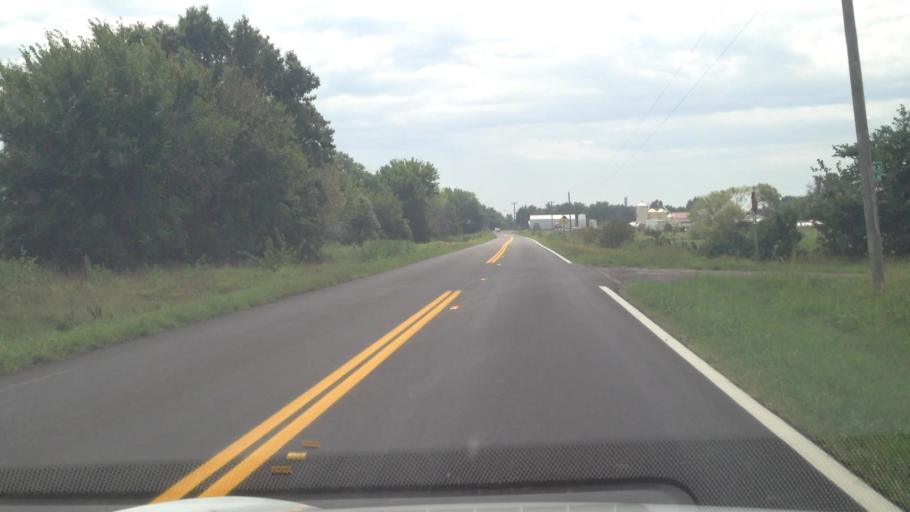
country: US
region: Kansas
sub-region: Crawford County
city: Girard
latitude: 37.6675
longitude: -94.9697
